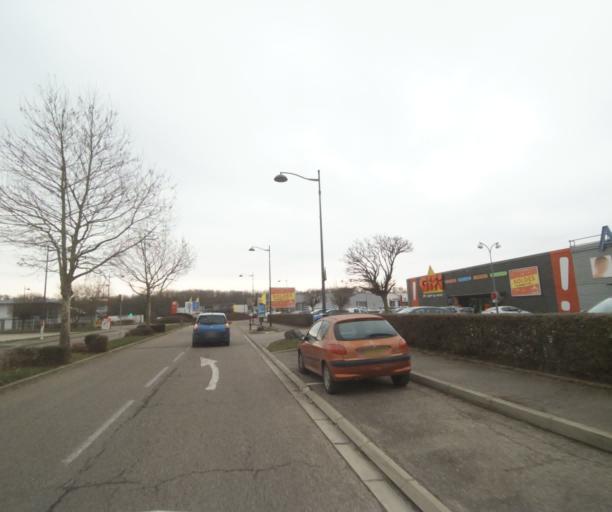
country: FR
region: Champagne-Ardenne
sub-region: Departement de la Haute-Marne
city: Saint-Dizier
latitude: 48.6248
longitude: 4.9688
